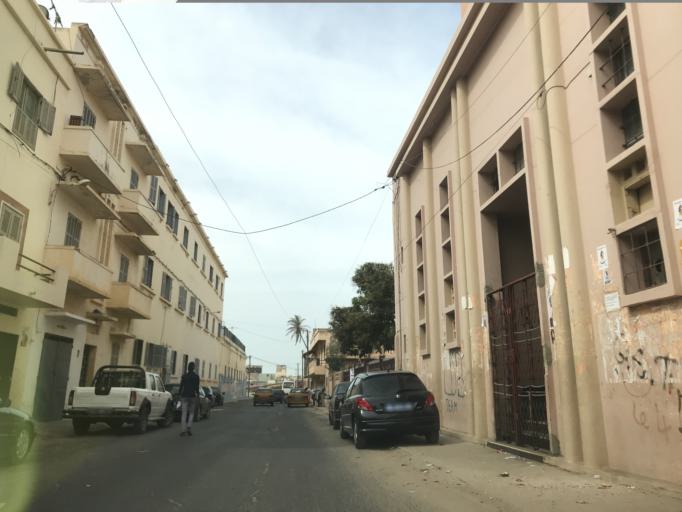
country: SN
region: Saint-Louis
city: Saint-Louis
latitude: 16.0268
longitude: -16.5052
